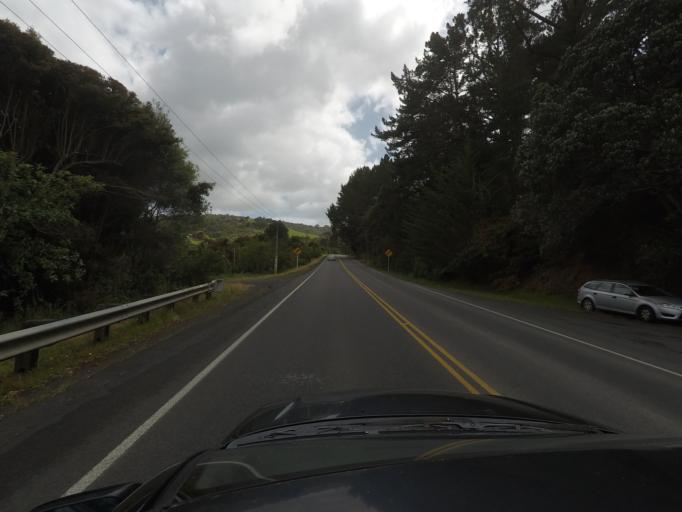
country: NZ
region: Auckland
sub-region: Auckland
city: Warkworth
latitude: -36.5611
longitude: 174.6965
